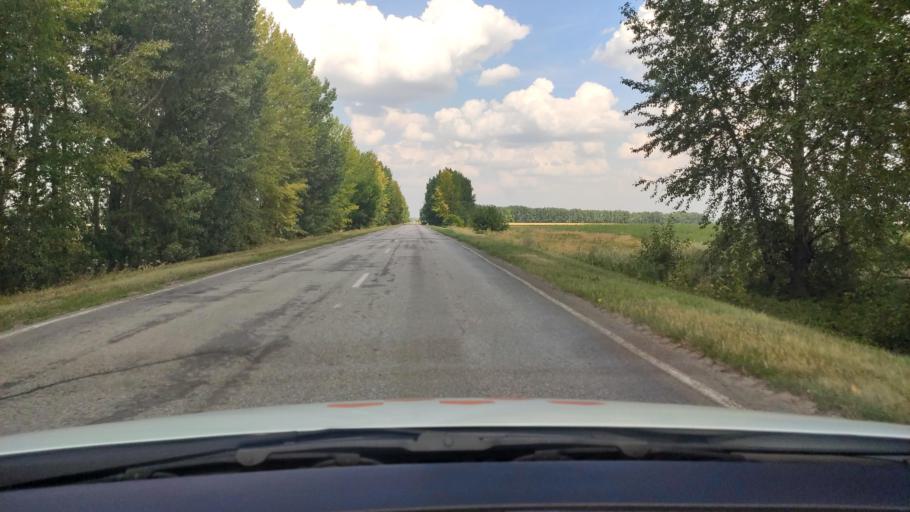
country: RU
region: Voronezj
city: Pereleshinskiy
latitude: 51.7305
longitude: 40.3790
